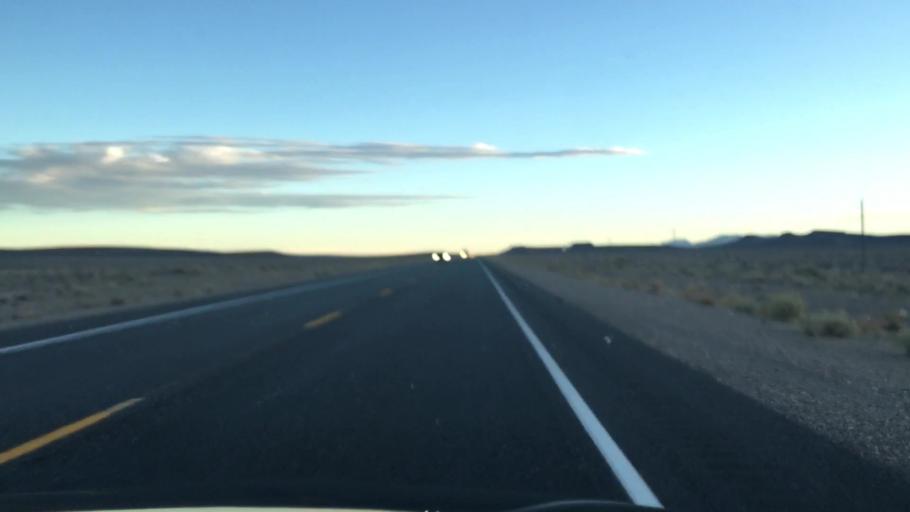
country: US
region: Nevada
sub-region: Esmeralda County
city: Goldfield
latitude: 37.4201
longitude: -117.1566
